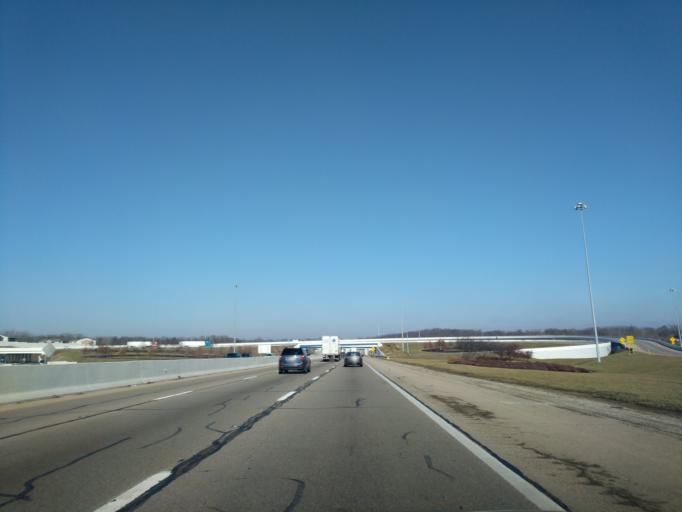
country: US
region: Ohio
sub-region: Montgomery County
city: Vandalia
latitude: 39.8620
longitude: -84.1890
